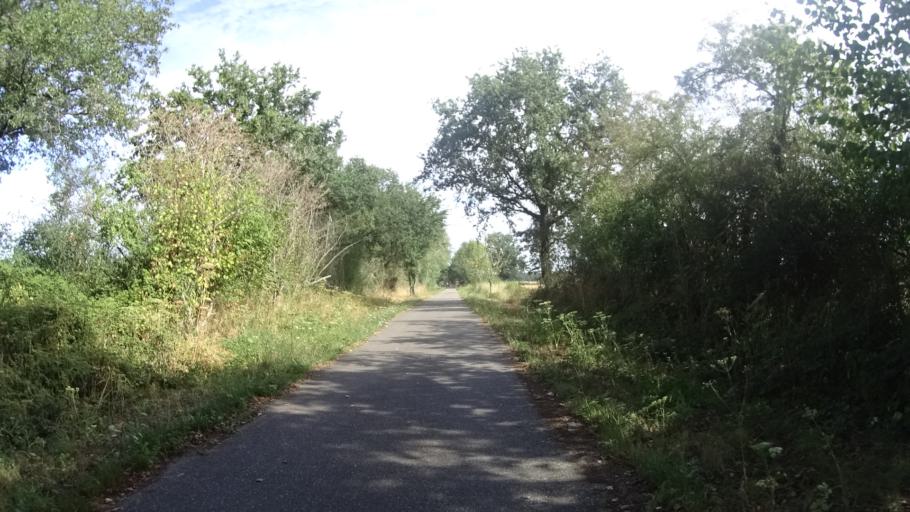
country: FR
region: Bourgogne
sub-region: Departement de Saone-et-Loire
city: Bourbon-Lancy
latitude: 46.5967
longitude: 3.7458
